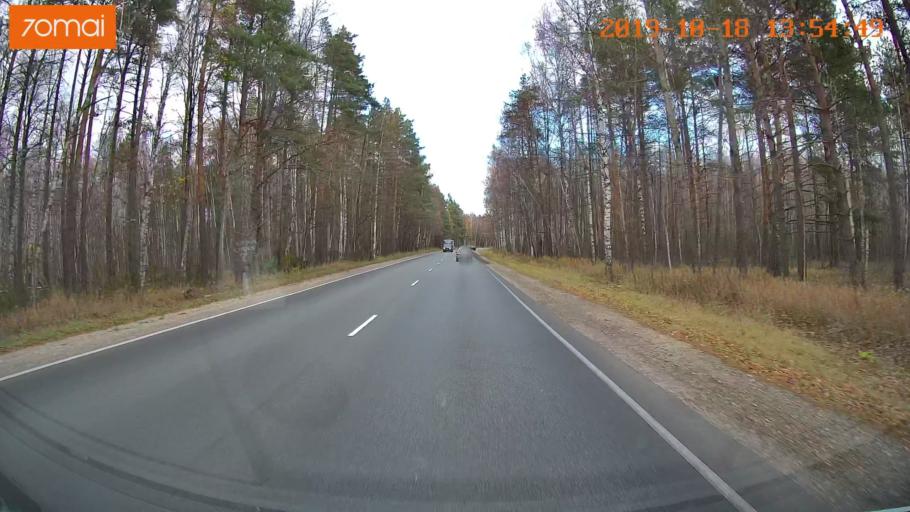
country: RU
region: Rjazan
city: Spas-Klepiki
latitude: 55.0470
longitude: 40.0152
